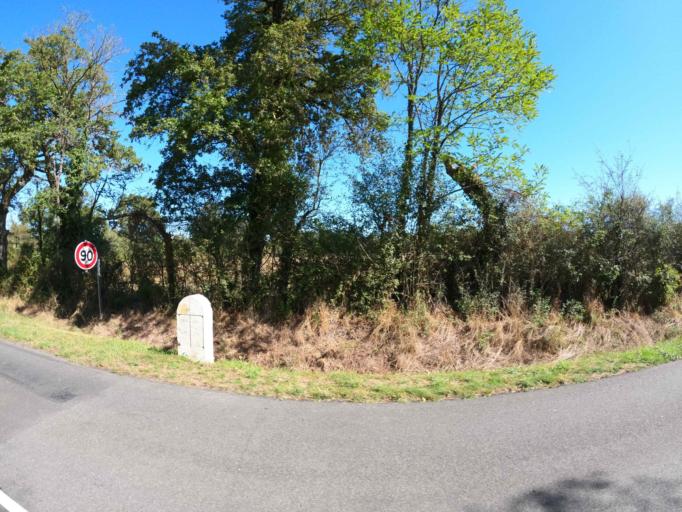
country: FR
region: Poitou-Charentes
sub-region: Departement de la Vienne
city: Lathus-Saint-Remy
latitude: 46.2883
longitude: 1.0053
